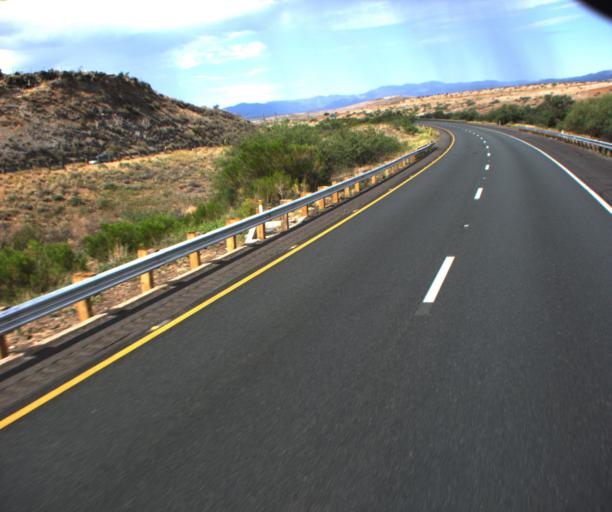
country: US
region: Arizona
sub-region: Yavapai County
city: Cordes Lakes
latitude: 34.4219
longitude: -112.0599
